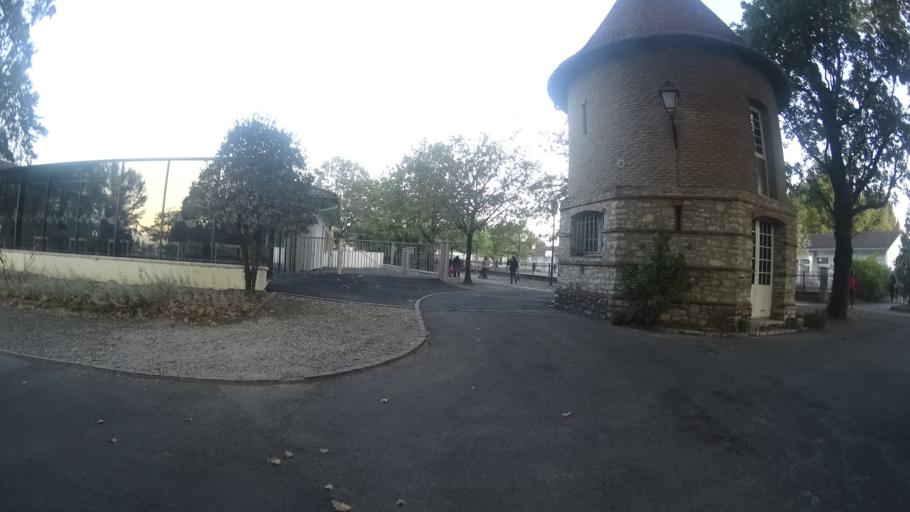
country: FR
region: Aquitaine
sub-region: Departement des Landes
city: Saint-Paul-les-Dax
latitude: 43.7248
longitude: -1.0516
